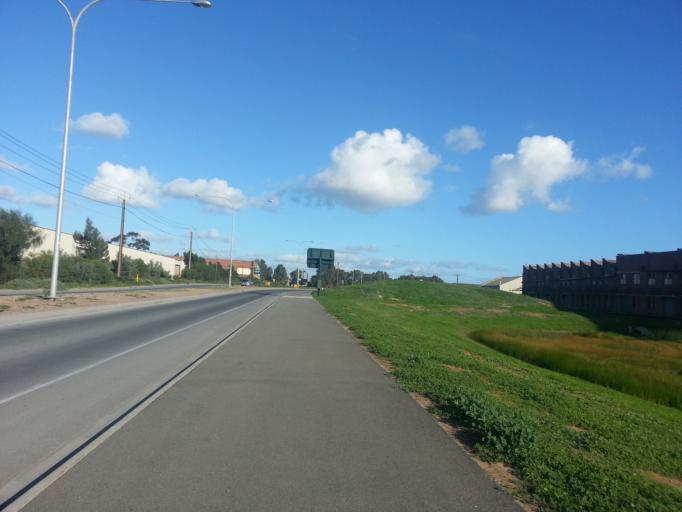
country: AU
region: South Australia
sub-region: Port Adelaide Enfield
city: Alberton
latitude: -34.8439
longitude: 138.5149
